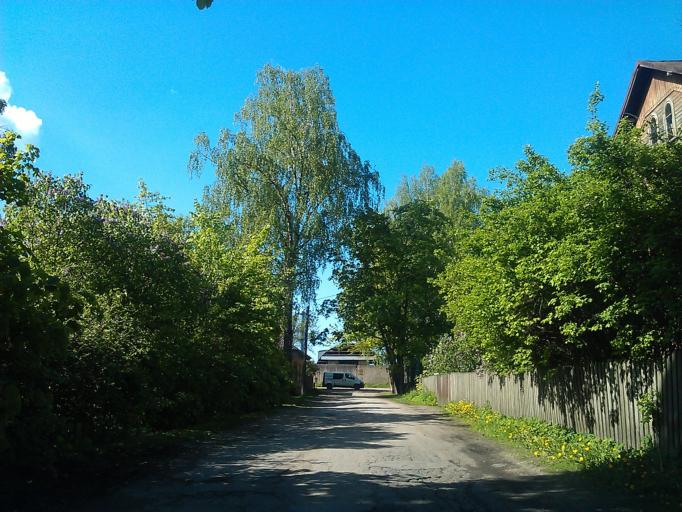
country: LV
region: Riga
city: Jaunciems
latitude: 56.9861
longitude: 24.1786
